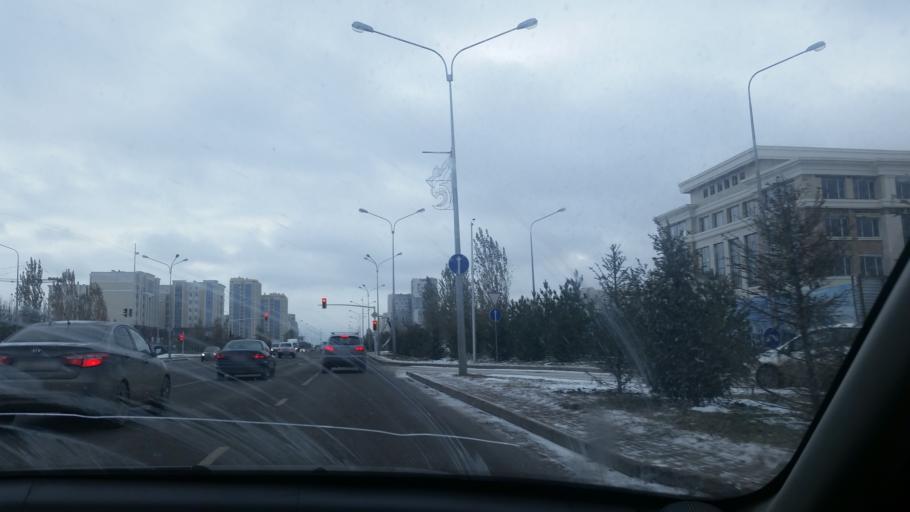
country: KZ
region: Astana Qalasy
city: Astana
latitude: 51.1010
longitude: 71.4288
